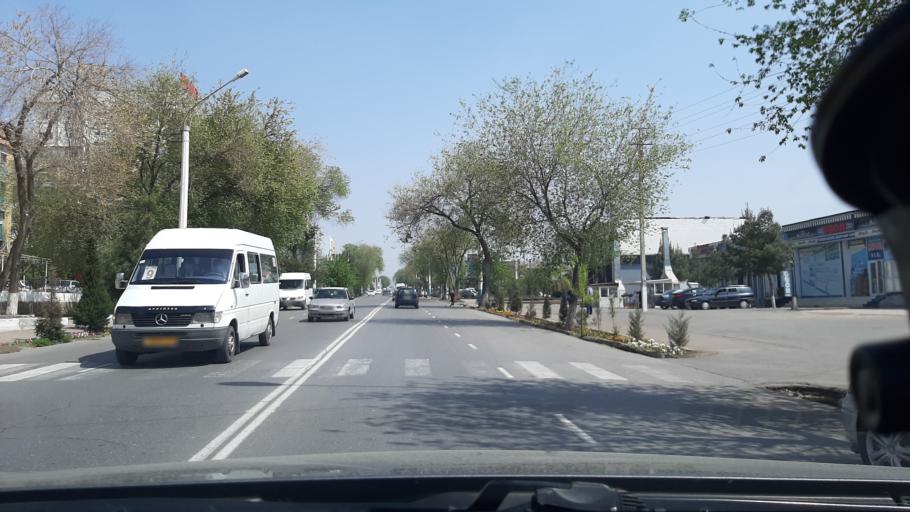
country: TJ
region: Viloyati Sughd
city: Khujand
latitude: 40.2960
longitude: 69.6098
